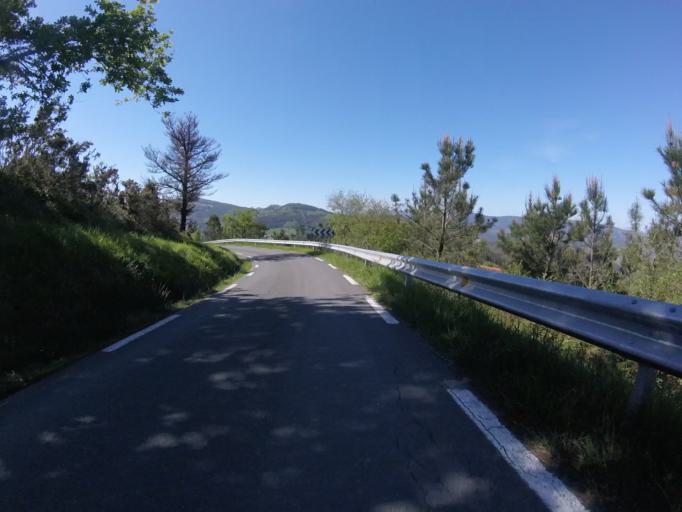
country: ES
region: Basque Country
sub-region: Provincia de Guipuzcoa
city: Errezil
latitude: 43.1891
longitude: -2.2065
